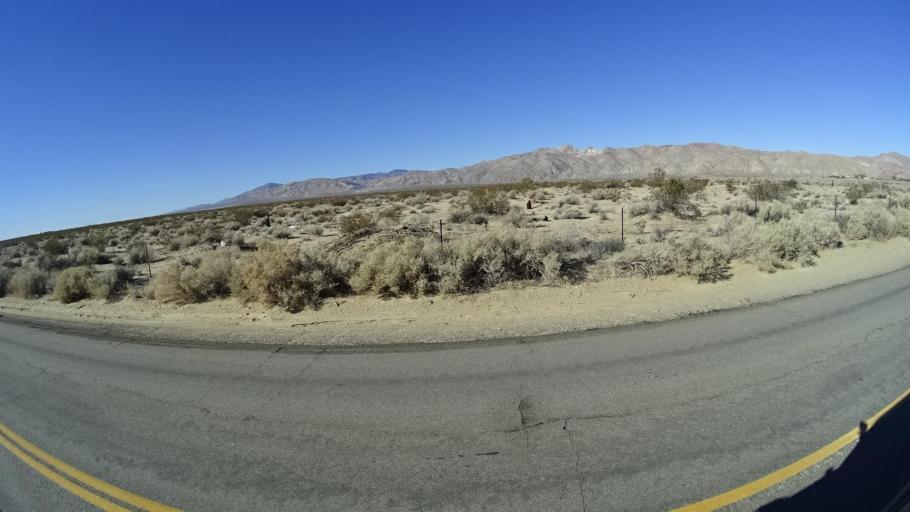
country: US
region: California
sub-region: Kern County
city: California City
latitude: 35.2490
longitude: -117.9859
